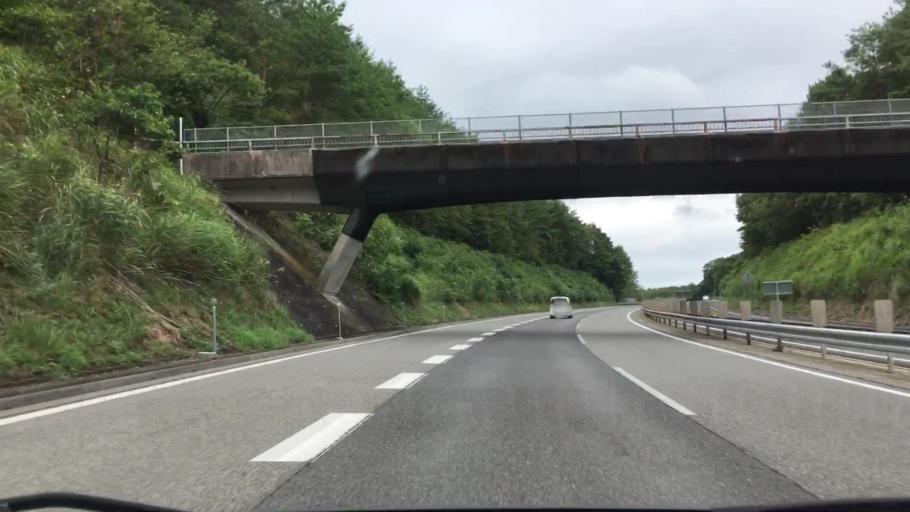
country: JP
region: Hiroshima
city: Miyoshi
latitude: 34.7535
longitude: 132.7615
